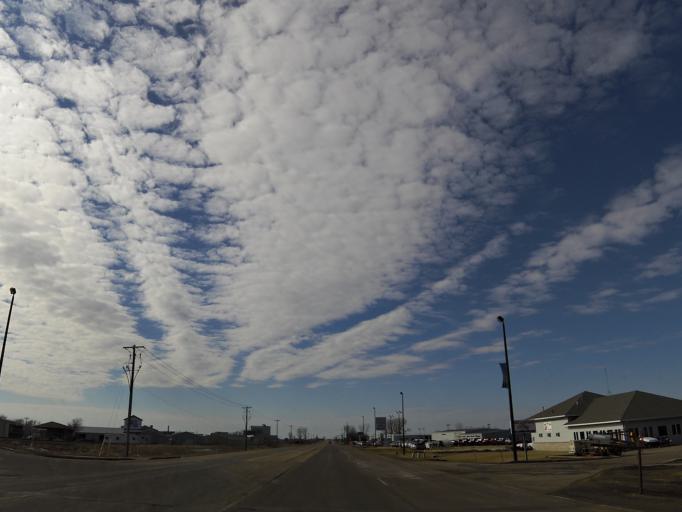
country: US
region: Minnesota
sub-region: Waseca County
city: Waseca
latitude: 44.0808
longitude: -93.5322
